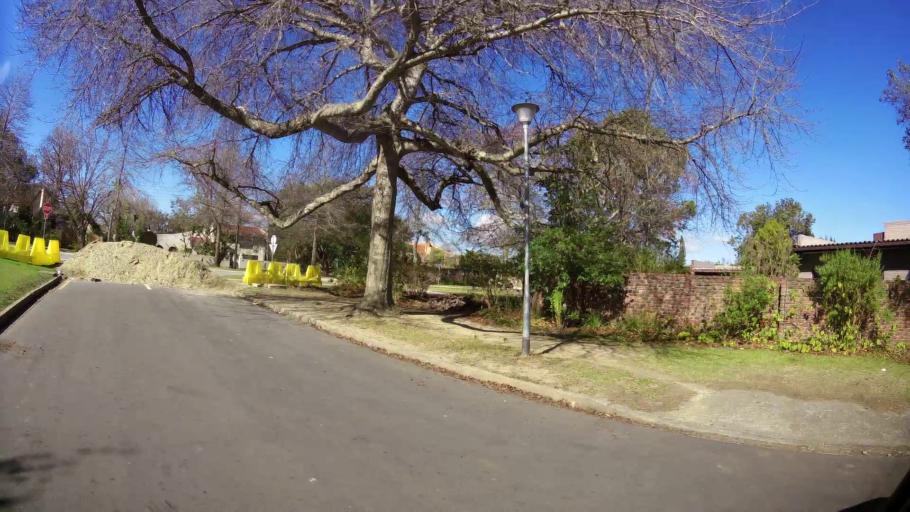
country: ZA
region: Western Cape
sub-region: Eden District Municipality
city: George
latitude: -33.9492
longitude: 22.4624
